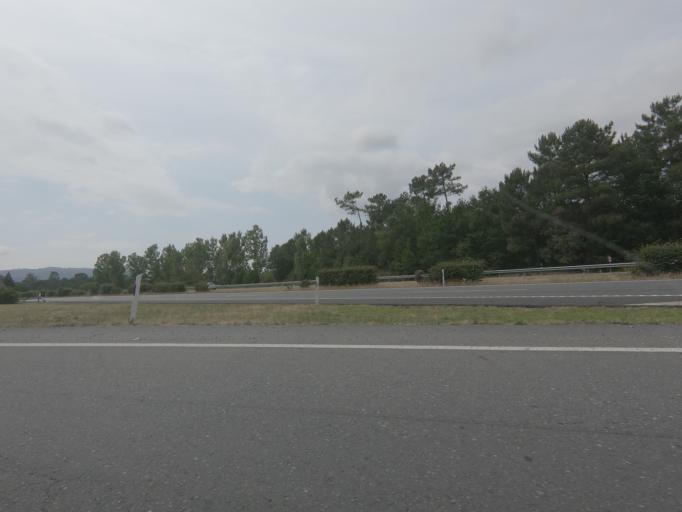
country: ES
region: Galicia
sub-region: Provincia de Pontevedra
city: Ponteareas
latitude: 42.1555
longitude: -8.4992
